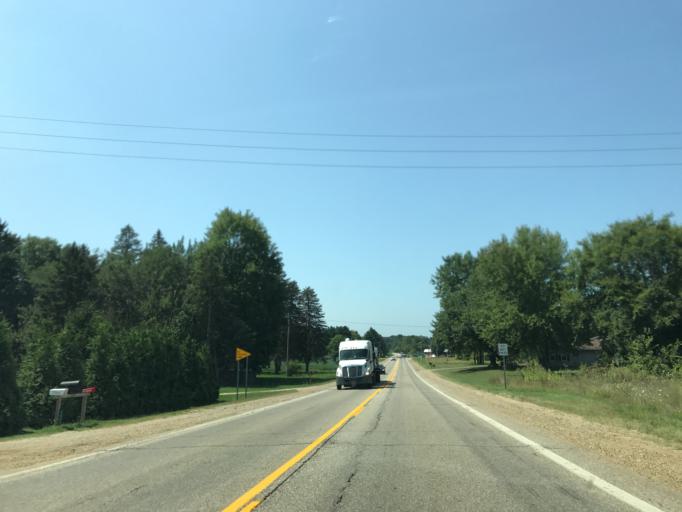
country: US
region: Michigan
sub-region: Berrien County
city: Buchanan
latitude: 41.8052
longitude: -86.3856
